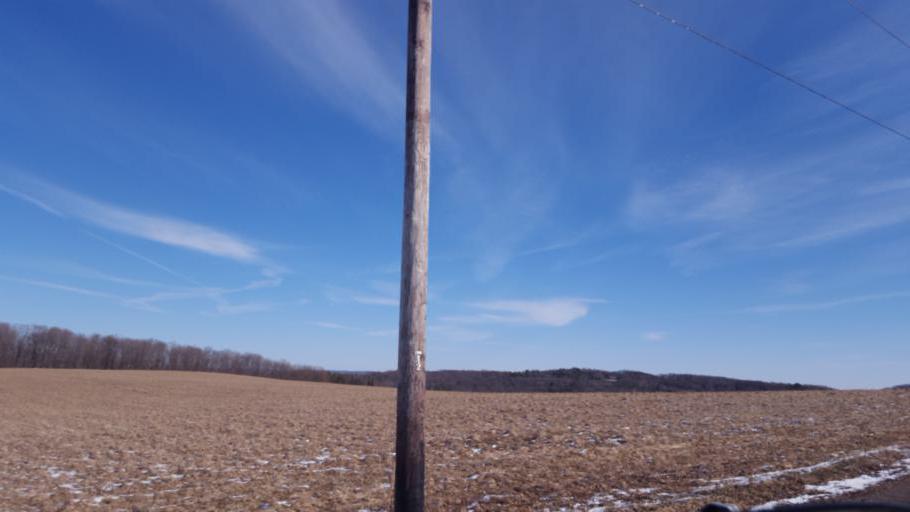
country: US
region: New York
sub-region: Allegany County
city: Wellsville
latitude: 42.1008
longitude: -77.9956
